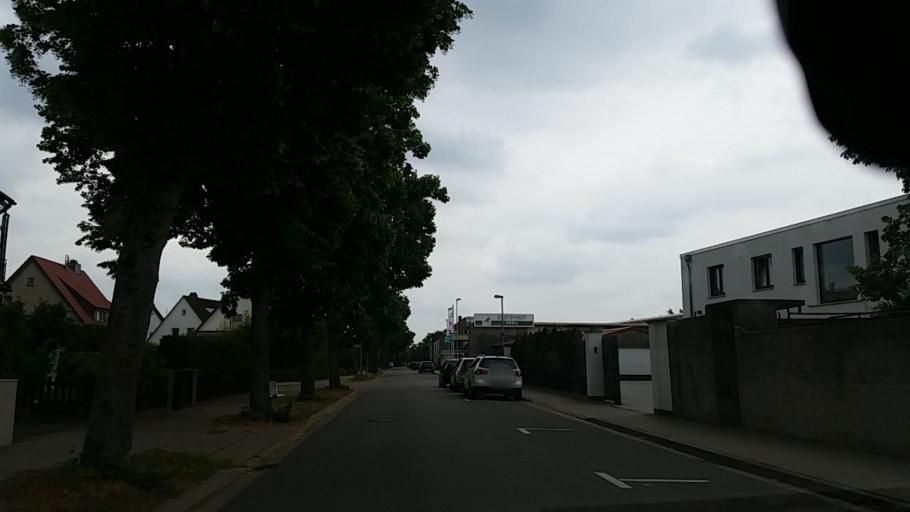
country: DE
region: Lower Saxony
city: Danndorf
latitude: 52.4319
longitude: 10.8558
